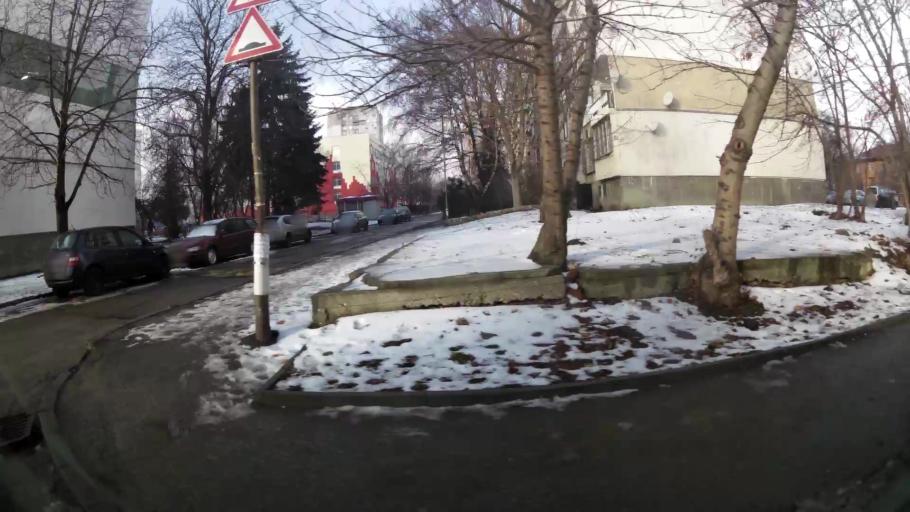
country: BG
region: Sofia-Capital
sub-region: Stolichna Obshtina
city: Sofia
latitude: 42.6990
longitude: 23.2801
